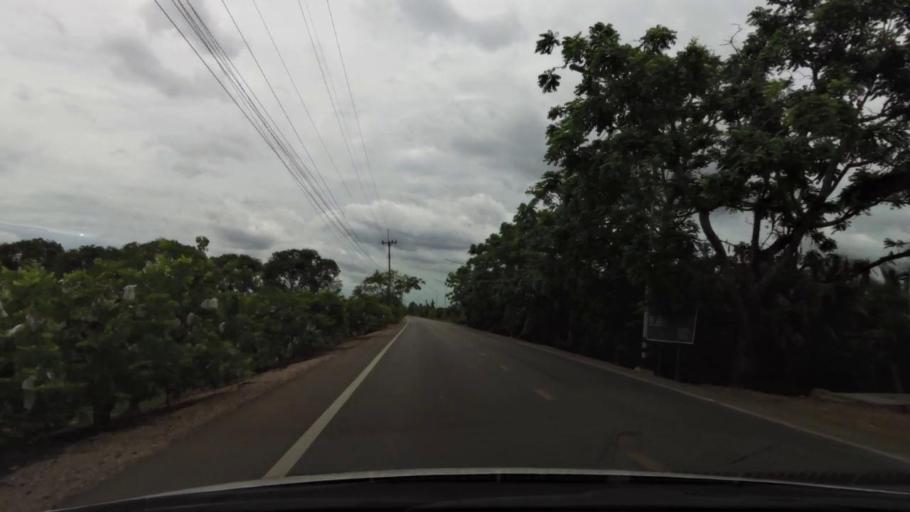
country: TH
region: Ratchaburi
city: Damnoen Saduak
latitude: 13.5608
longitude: 100.0136
